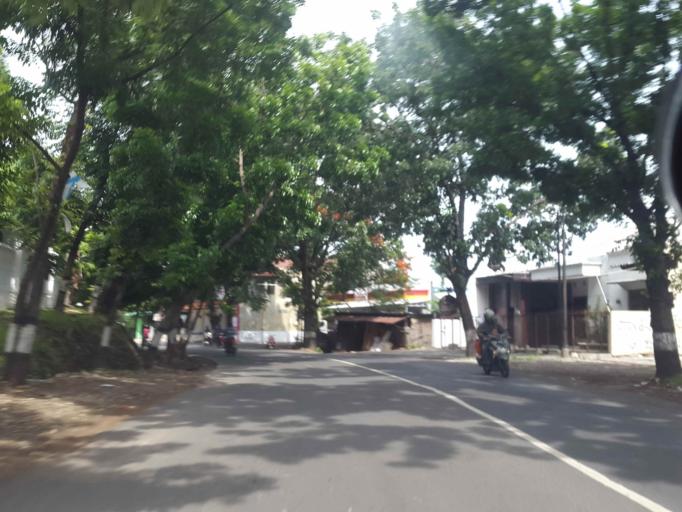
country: ID
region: Central Java
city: Semarang
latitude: -7.0038
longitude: 110.3809
